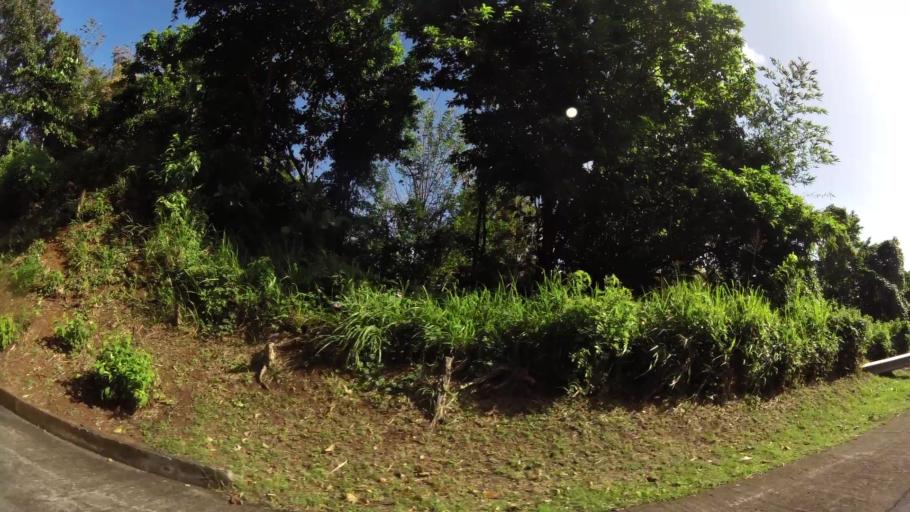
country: MQ
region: Martinique
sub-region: Martinique
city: Sainte-Marie
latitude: 14.7792
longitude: -60.9915
